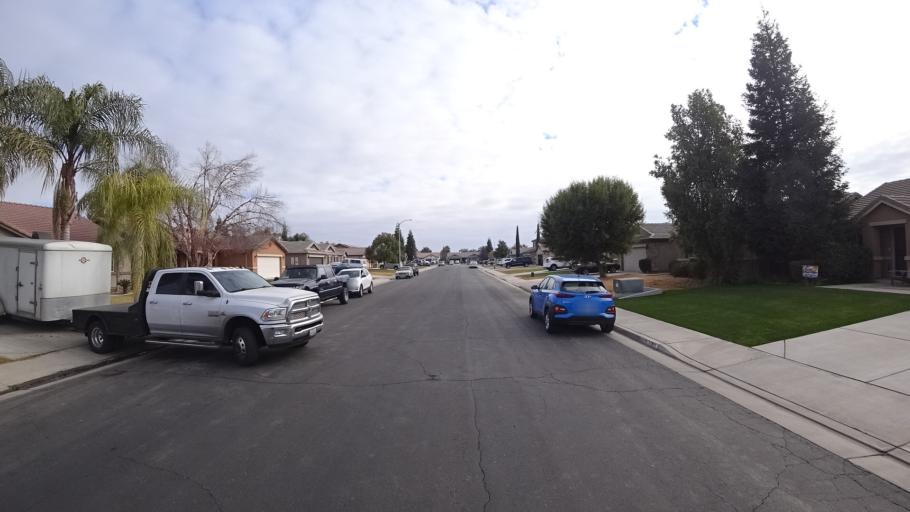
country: US
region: California
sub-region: Kern County
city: Rosedale
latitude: 35.3022
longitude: -119.1347
